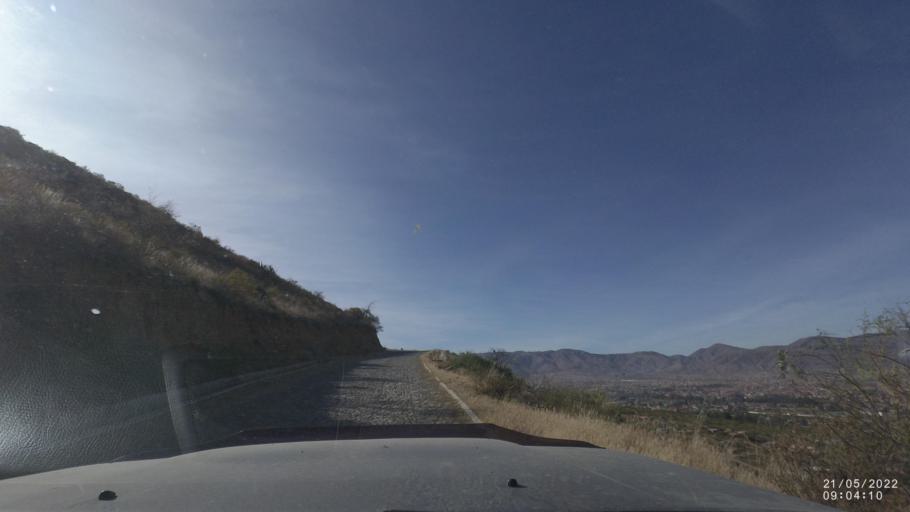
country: BO
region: Cochabamba
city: Cochabamba
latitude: -17.3792
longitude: -66.0273
